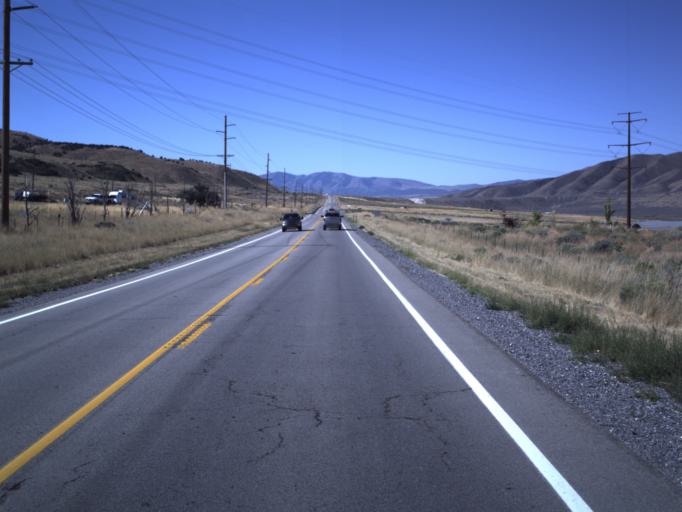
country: US
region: Utah
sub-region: Tooele County
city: Tooele
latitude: 40.4941
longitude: -112.3307
